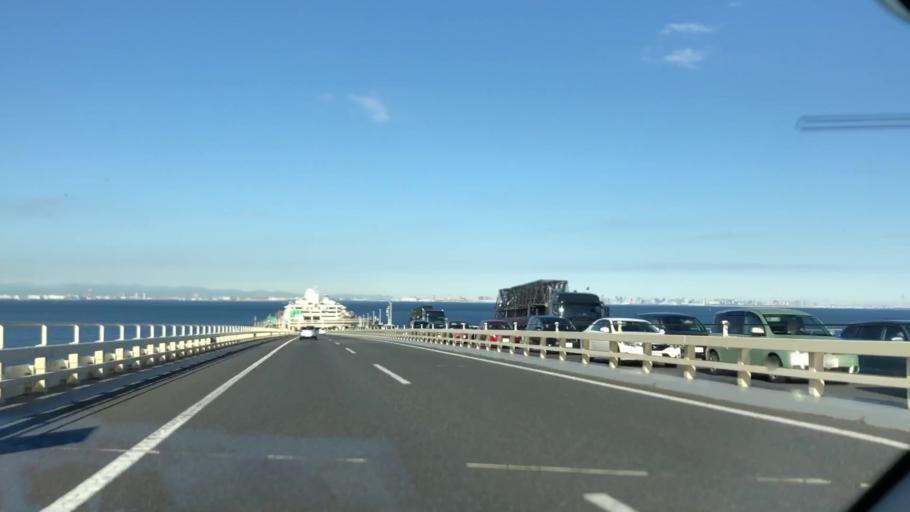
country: JP
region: Chiba
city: Kisarazu
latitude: 35.4581
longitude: 139.8836
